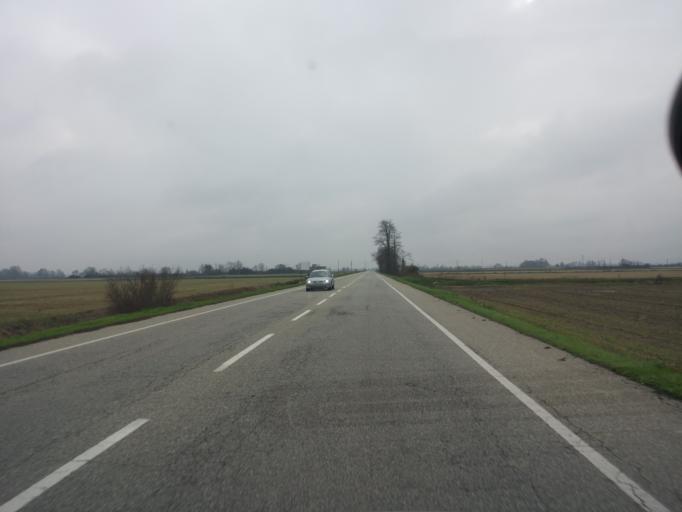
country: IT
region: Piedmont
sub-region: Provincia di Vercelli
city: Stroppiana
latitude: 45.2126
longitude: 8.4580
